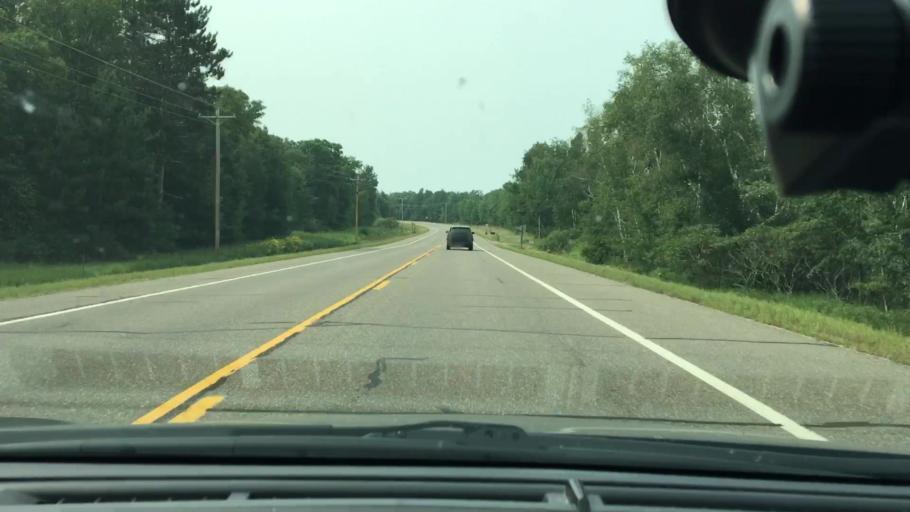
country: US
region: Minnesota
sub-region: Crow Wing County
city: Breezy Point
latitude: 46.5633
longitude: -94.1320
